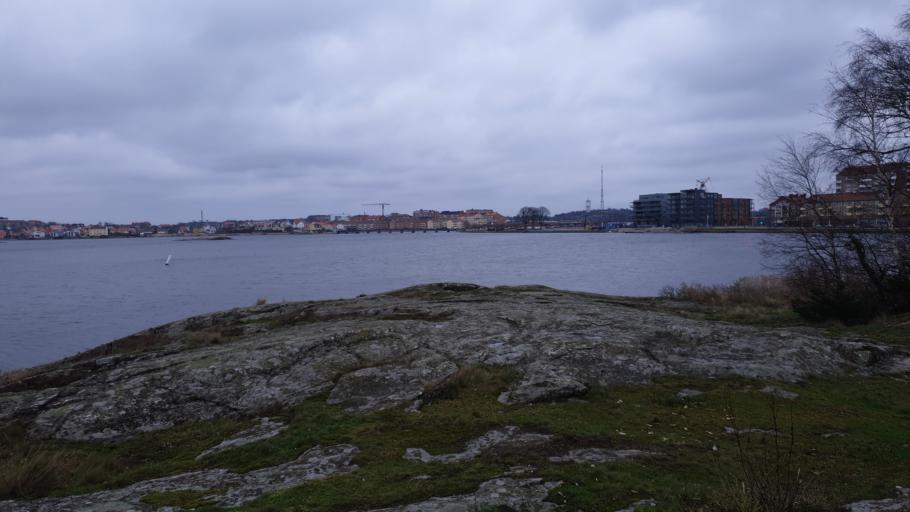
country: SE
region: Blekinge
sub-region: Karlskrona Kommun
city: Karlskrona
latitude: 56.1644
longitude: 15.5761
